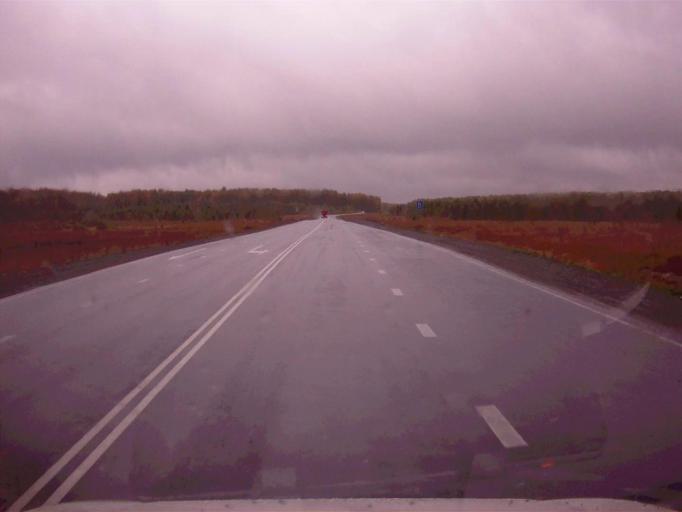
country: RU
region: Chelyabinsk
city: Tayginka
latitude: 55.5032
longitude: 60.6366
